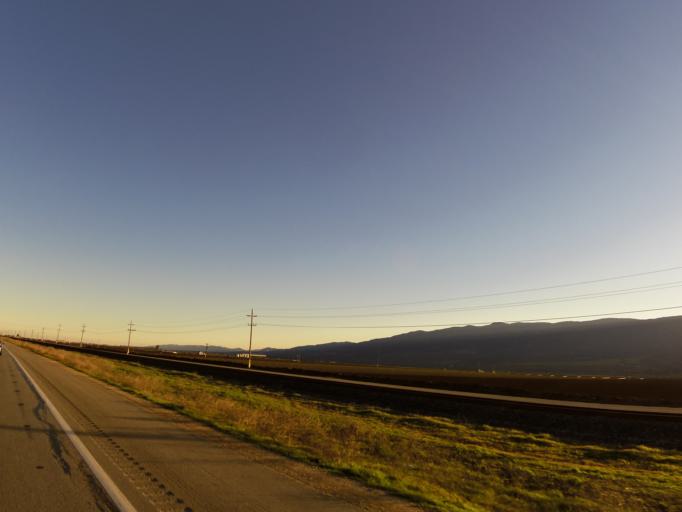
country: US
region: California
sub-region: Monterey County
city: Gonzales
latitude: 36.4825
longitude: -121.4161
